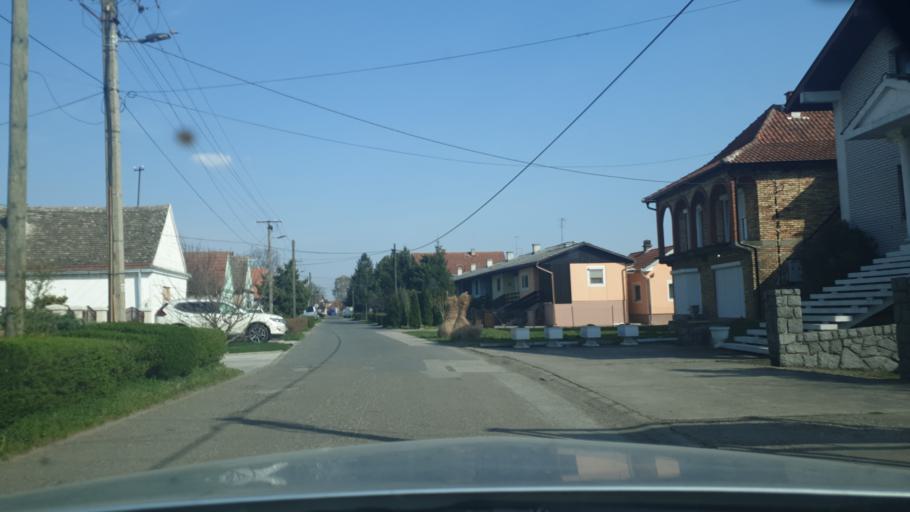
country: RS
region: Autonomna Pokrajina Vojvodina
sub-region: Sremski Okrug
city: Stara Pazova
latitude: 44.9785
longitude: 20.1527
